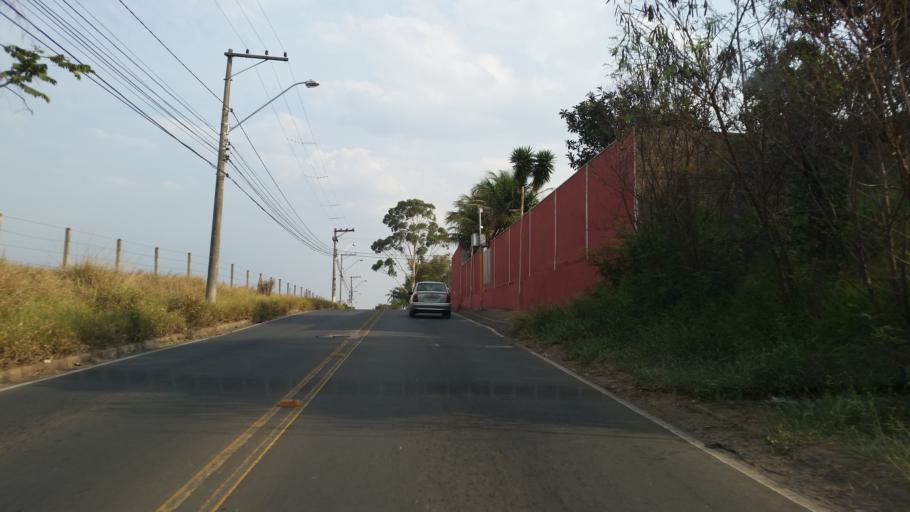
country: BR
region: Sao Paulo
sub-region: Hortolandia
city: Hortolandia
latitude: -22.9263
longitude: -47.1892
